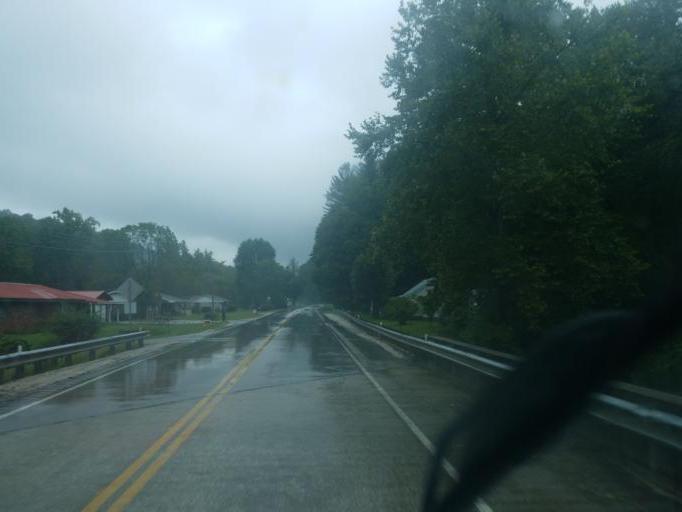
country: US
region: Kentucky
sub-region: Rowan County
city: Morehead
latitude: 38.2434
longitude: -83.3454
